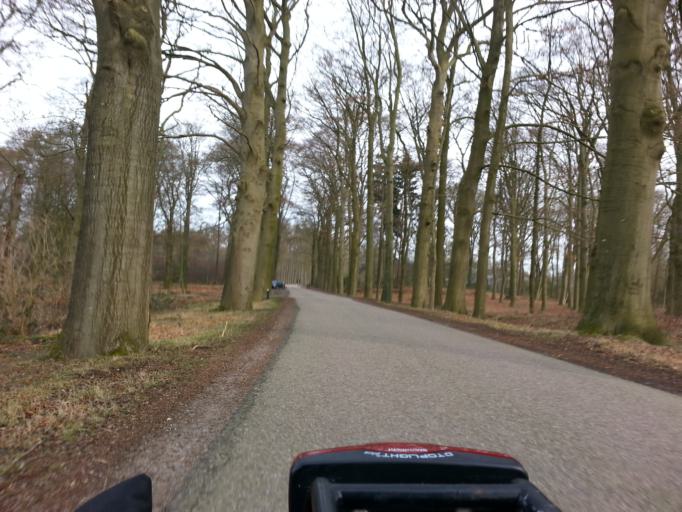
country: NL
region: Utrecht
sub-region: Gemeente Woudenberg
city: Woudenberg
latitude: 52.0995
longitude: 5.3898
